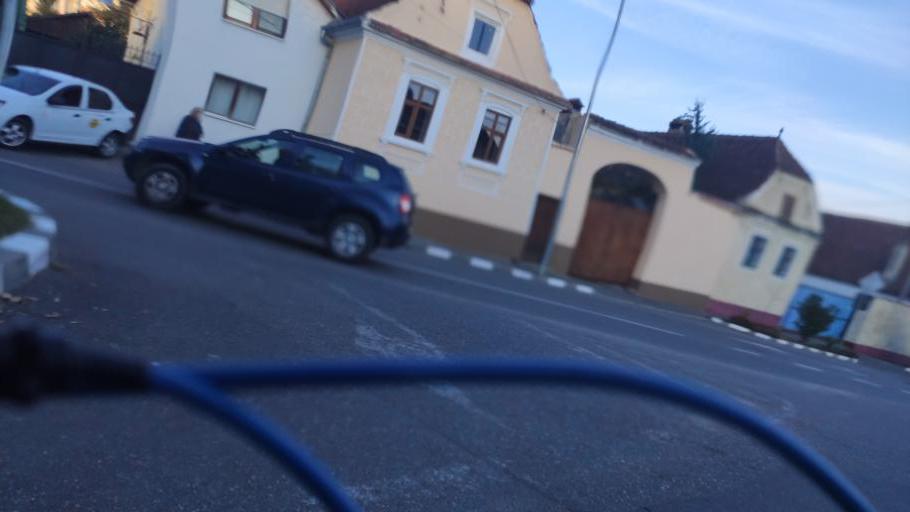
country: RO
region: Brasov
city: Codlea
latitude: 45.7020
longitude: 25.4411
